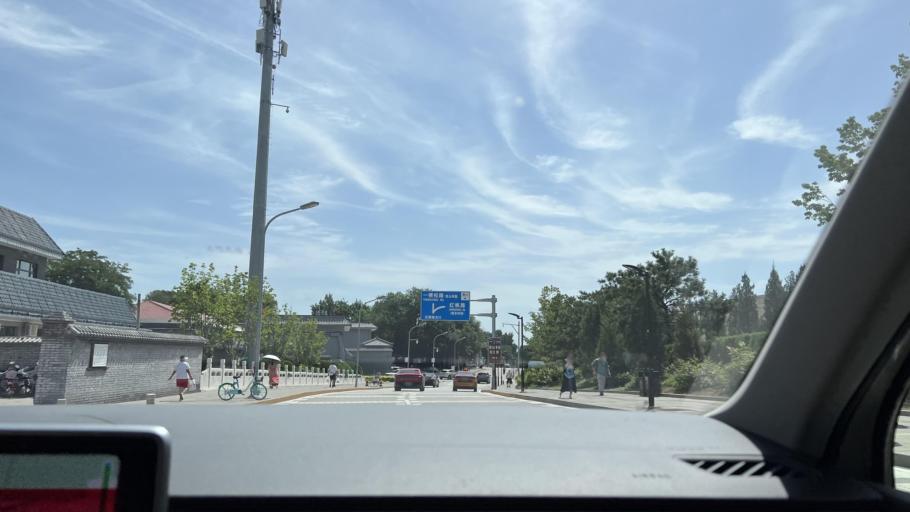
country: CN
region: Beijing
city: Xiangshan
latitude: 39.9922
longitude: 116.1987
